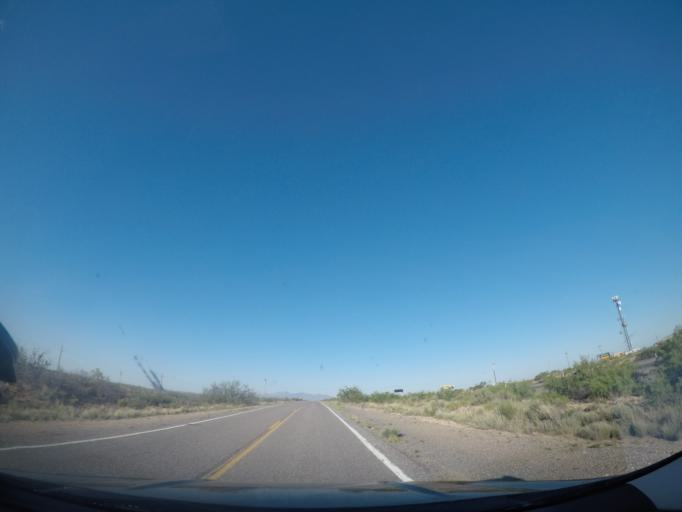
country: US
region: New Mexico
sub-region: Dona Ana County
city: Mesilla
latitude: 32.2661
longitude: -106.9789
